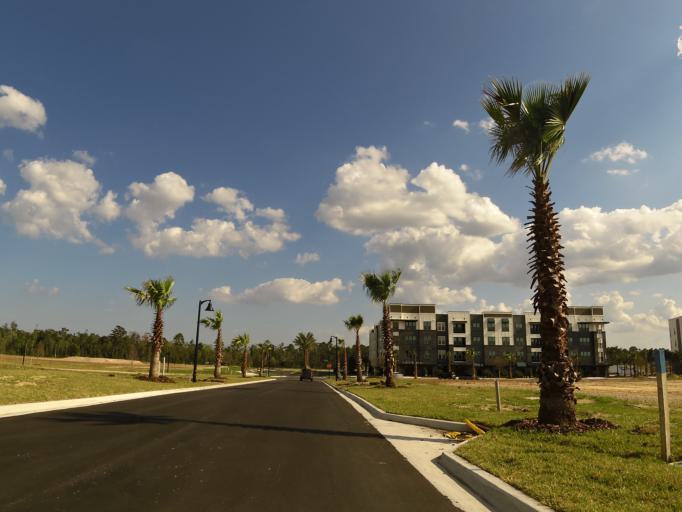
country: US
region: Florida
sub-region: Saint Johns County
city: Palm Valley
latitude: 30.1663
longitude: -81.5078
